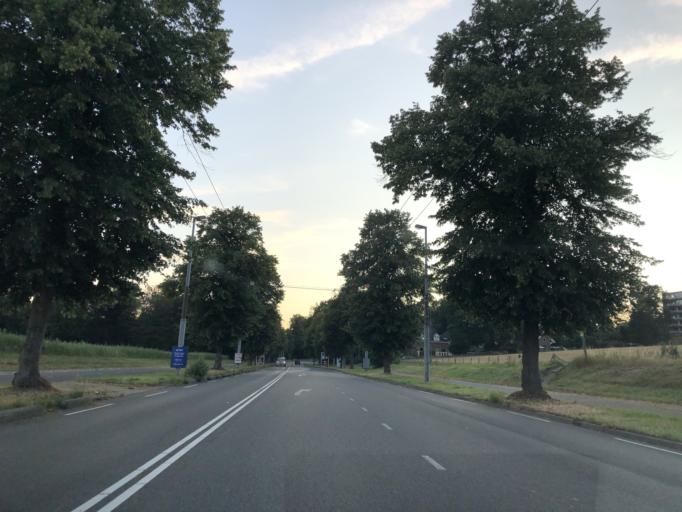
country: NL
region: Gelderland
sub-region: Gemeente Renkum
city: Oosterbeek
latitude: 51.9855
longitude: 5.8609
